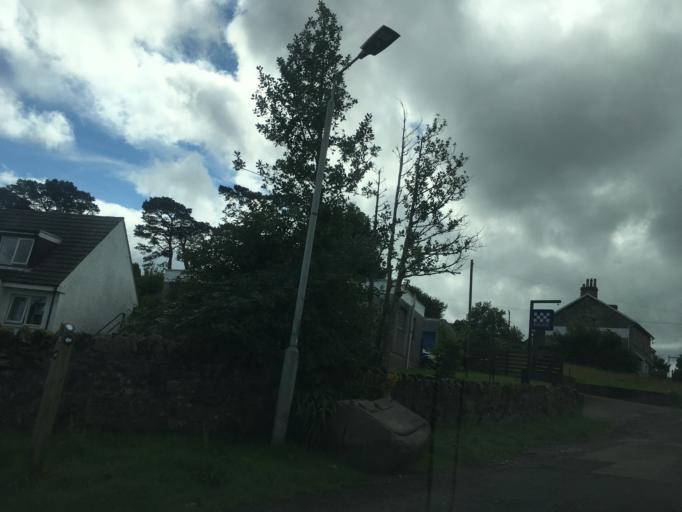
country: GB
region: Scotland
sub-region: Argyll and Bute
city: Tarbert
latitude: 55.8928
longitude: -5.2451
